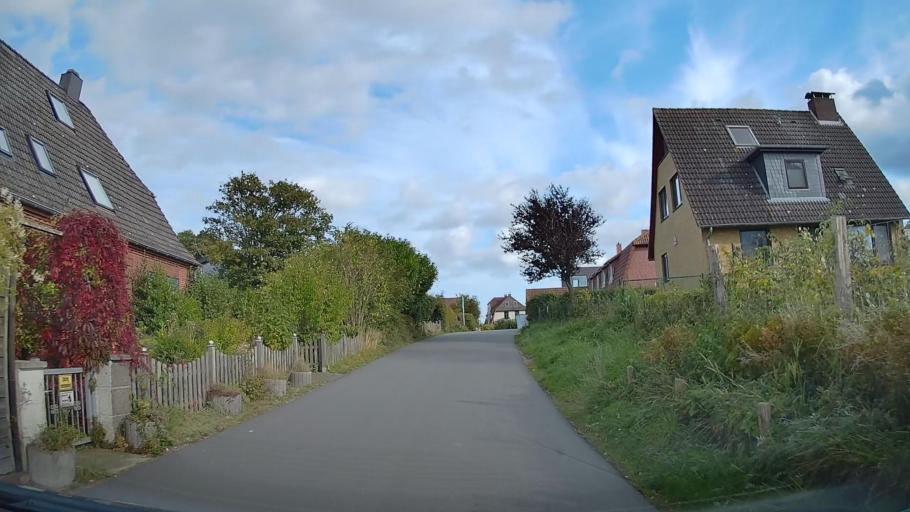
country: DE
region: Schleswig-Holstein
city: Pommerby
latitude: 54.7687
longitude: 9.9602
